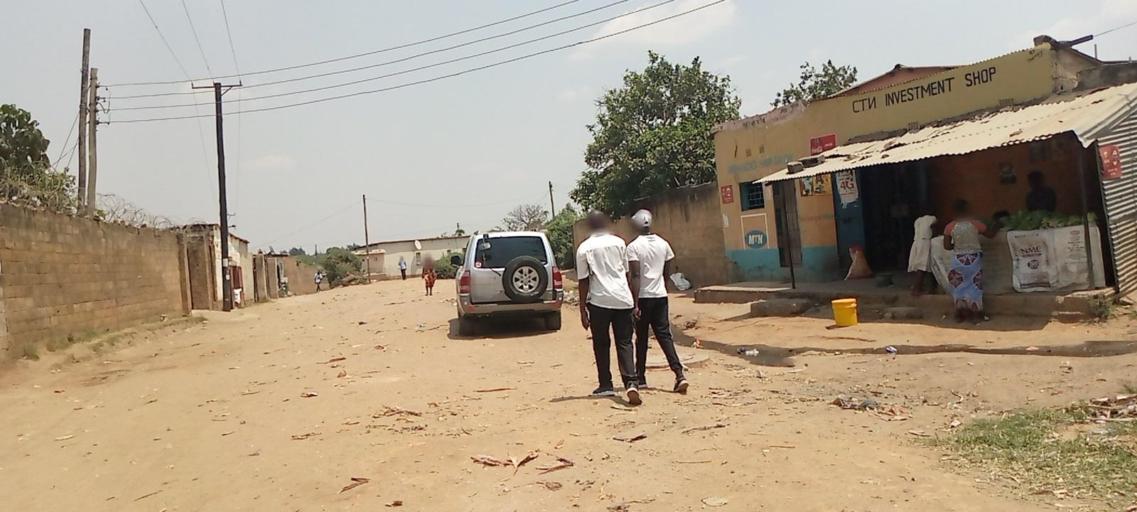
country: ZM
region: Lusaka
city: Lusaka
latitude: -15.4010
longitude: 28.3464
